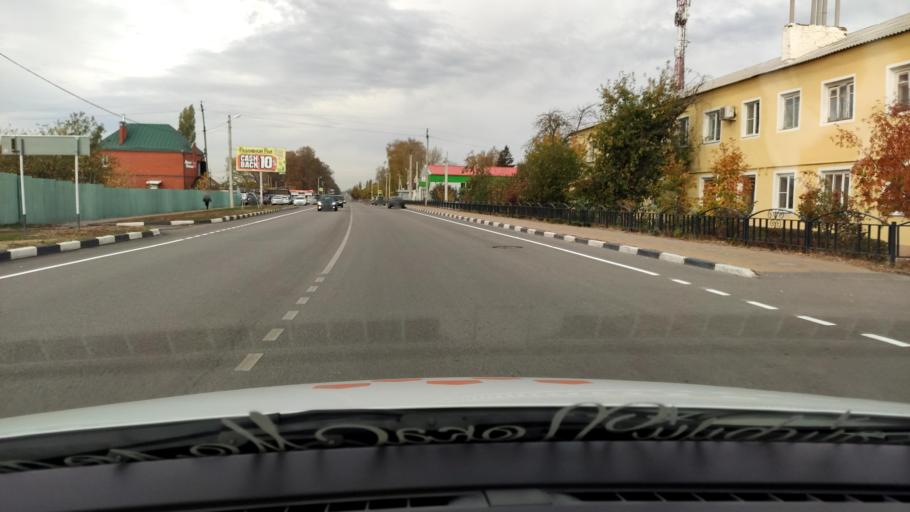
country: RU
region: Voronezj
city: Ramon'
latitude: 51.9096
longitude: 39.3345
